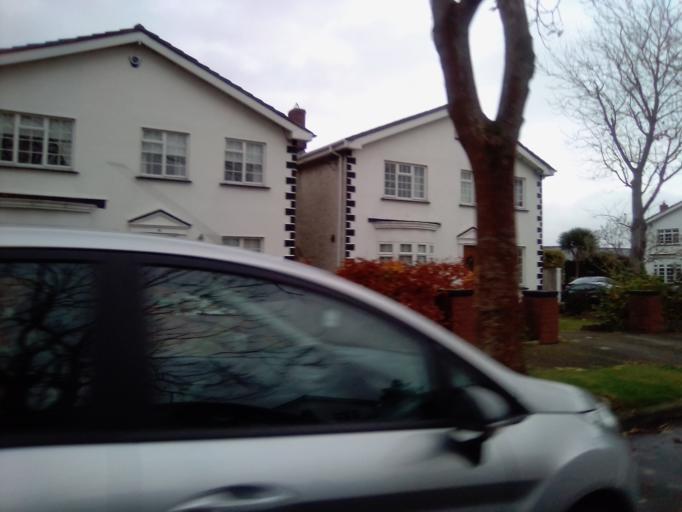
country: IE
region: Leinster
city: Malahide
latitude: 53.4480
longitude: -6.1382
